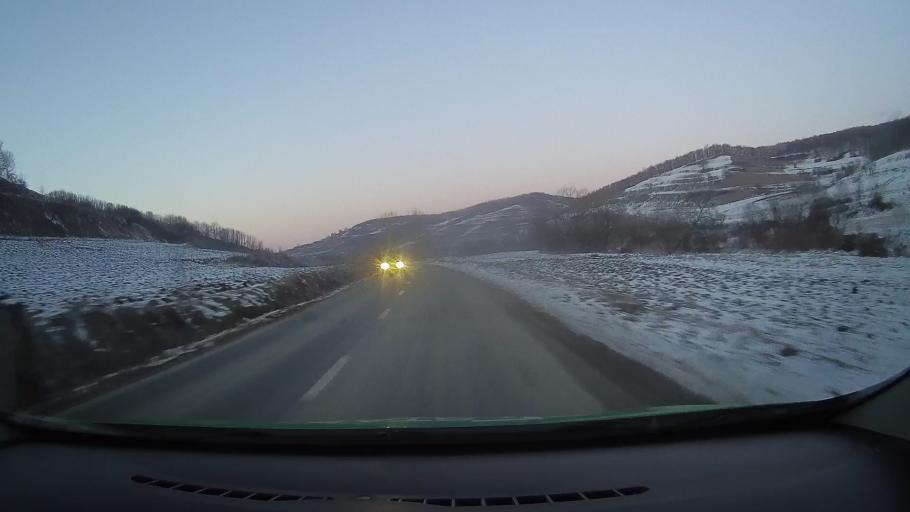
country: RO
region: Sibiu
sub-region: Comuna Atel
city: Atel
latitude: 46.1721
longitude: 24.4699
